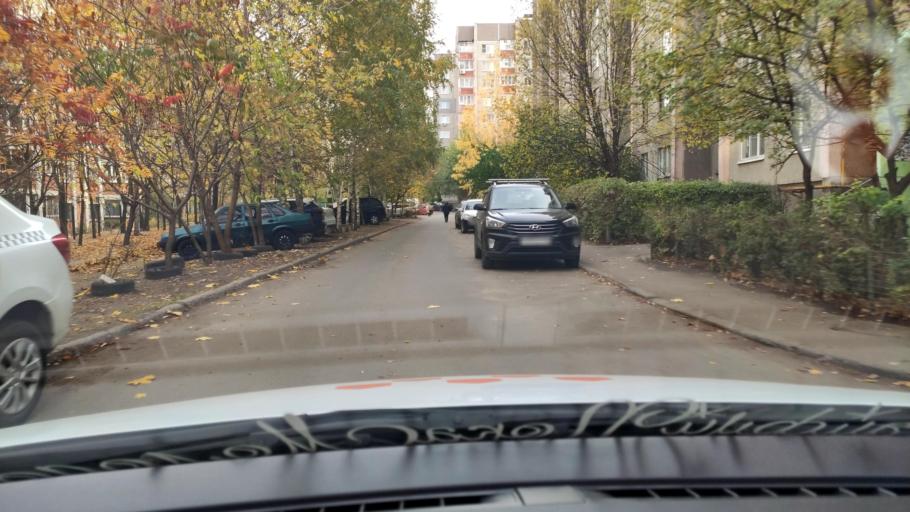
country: RU
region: Voronezj
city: Podgornoye
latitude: 51.7095
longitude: 39.1453
